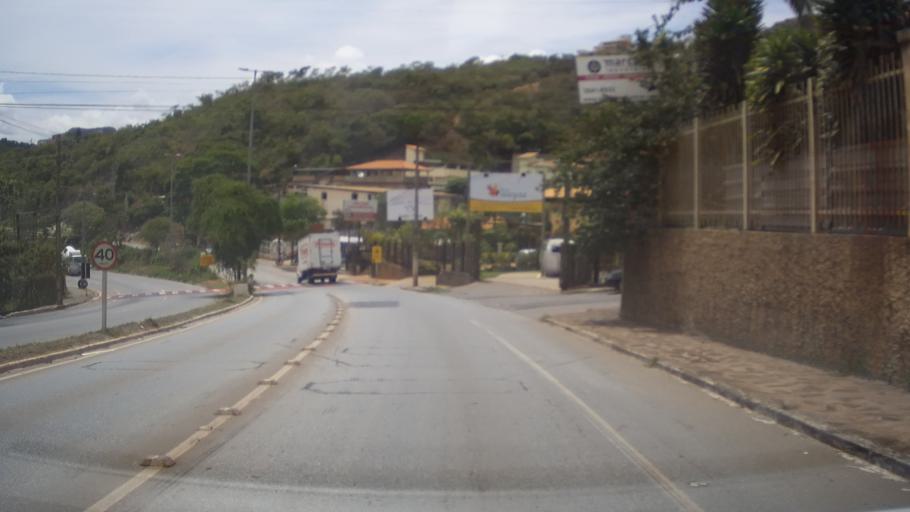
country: BR
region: Minas Gerais
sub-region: Nova Lima
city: Nova Lima
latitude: -19.9998
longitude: -43.8881
